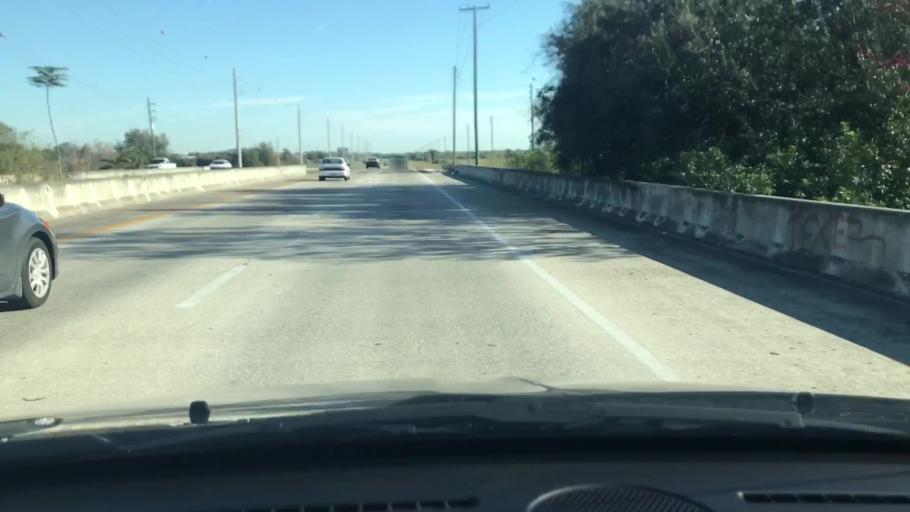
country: US
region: Florida
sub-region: Osceola County
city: Campbell
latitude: 28.2686
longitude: -81.4267
